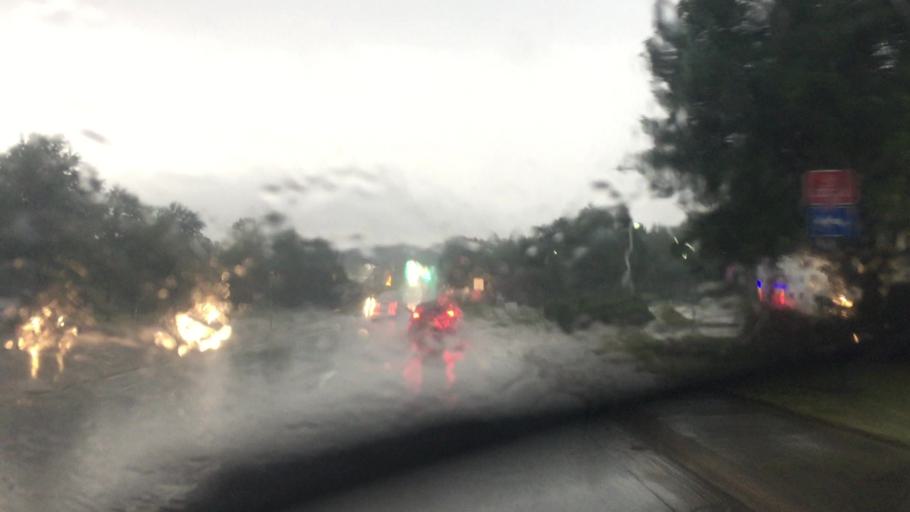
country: US
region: North Carolina
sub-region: Rowan County
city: Salisbury
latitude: 35.6441
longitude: -80.4844
